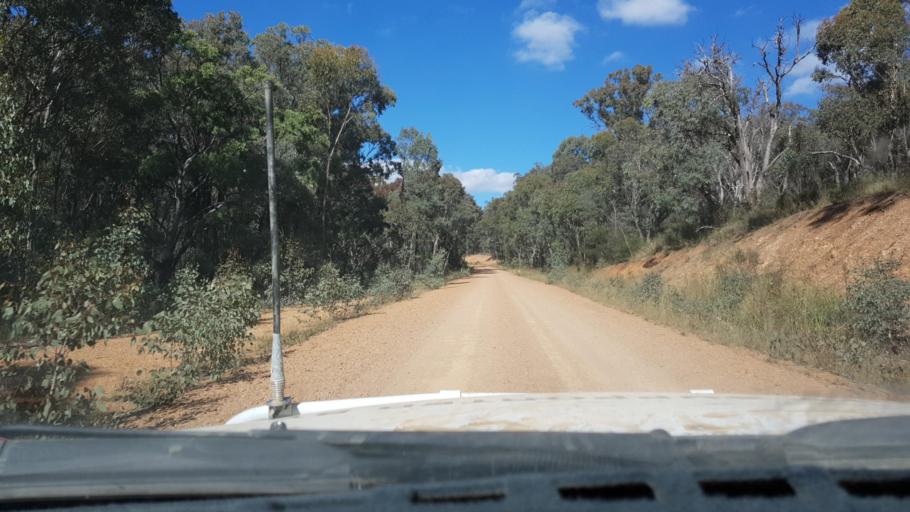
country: AU
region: New South Wales
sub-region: Tamworth Municipality
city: Manilla
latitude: -30.4518
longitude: 150.8768
